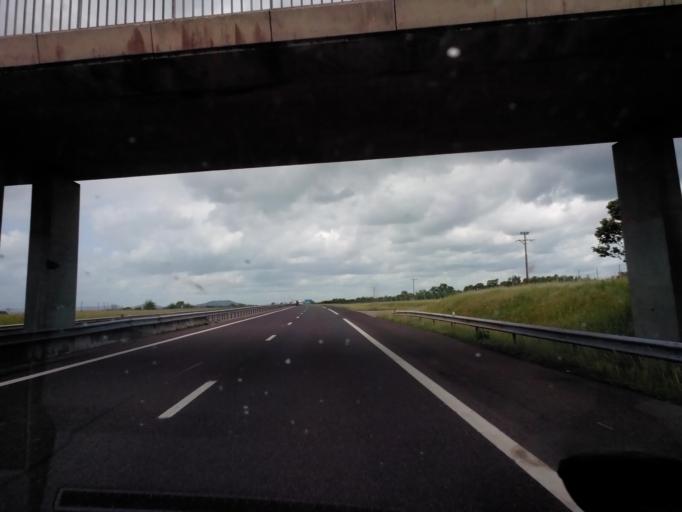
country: FR
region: Lorraine
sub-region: Departement de Meurthe-et-Moselle
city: Blenod-les-Toul
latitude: 48.5844
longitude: 5.8877
